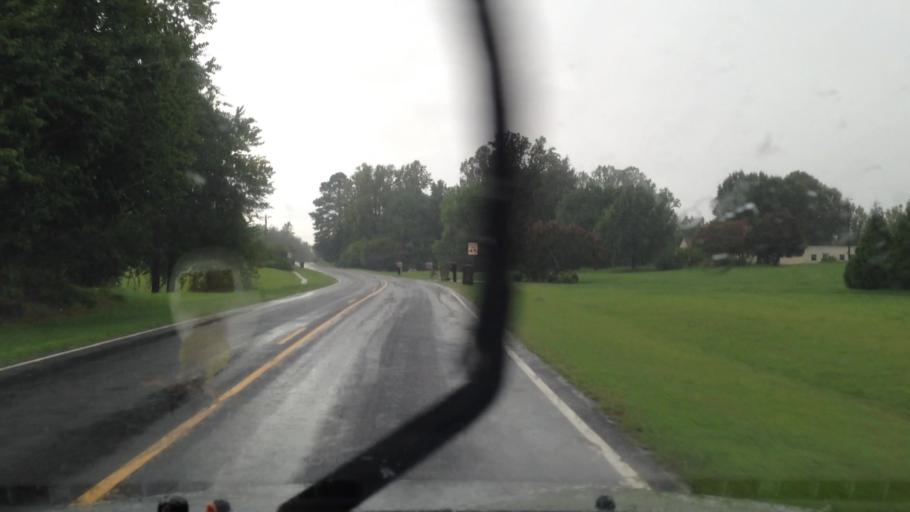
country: US
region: North Carolina
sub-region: Guilford County
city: Stokesdale
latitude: 36.2171
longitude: -80.0296
